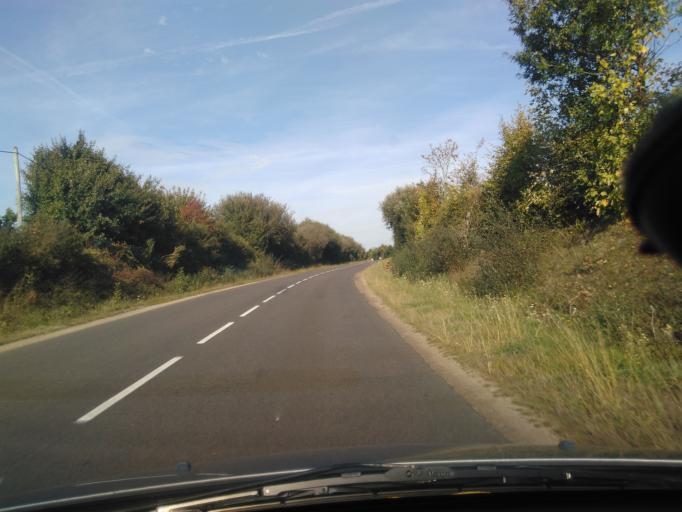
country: FR
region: Pays de la Loire
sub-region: Departement de la Vendee
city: Nieul-le-Dolent
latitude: 46.5594
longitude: -1.5171
